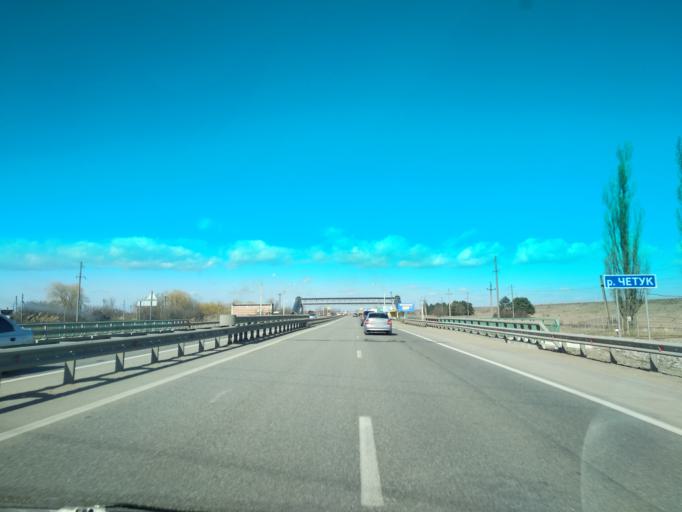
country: RU
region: Adygeya
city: Adygeysk
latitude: 44.9108
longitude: 39.1530
